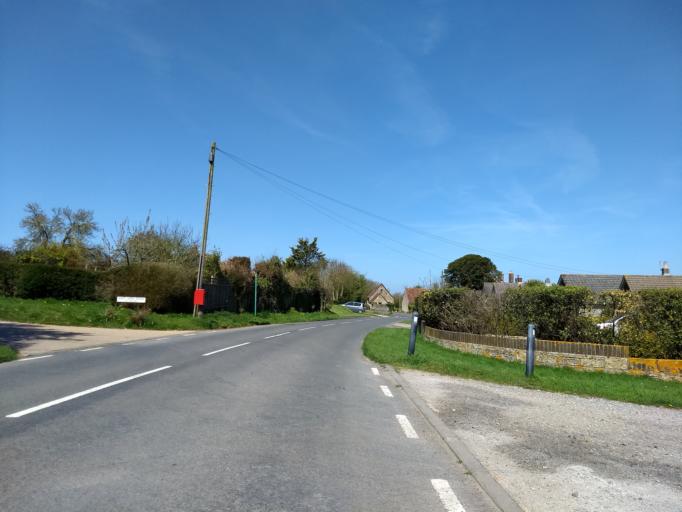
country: GB
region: England
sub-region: Isle of Wight
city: Gurnard
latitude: 50.7454
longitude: -1.3332
